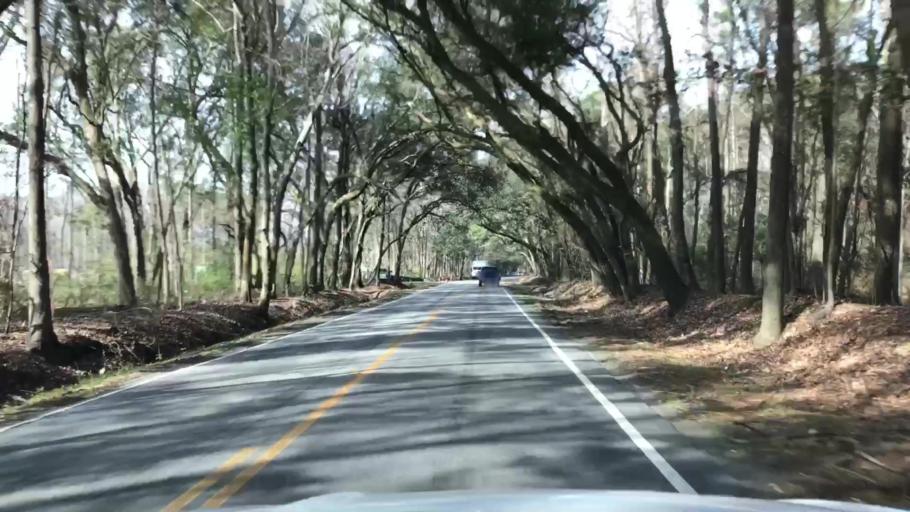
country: US
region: South Carolina
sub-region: Charleston County
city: Shell Point
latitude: 32.7566
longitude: -80.0517
